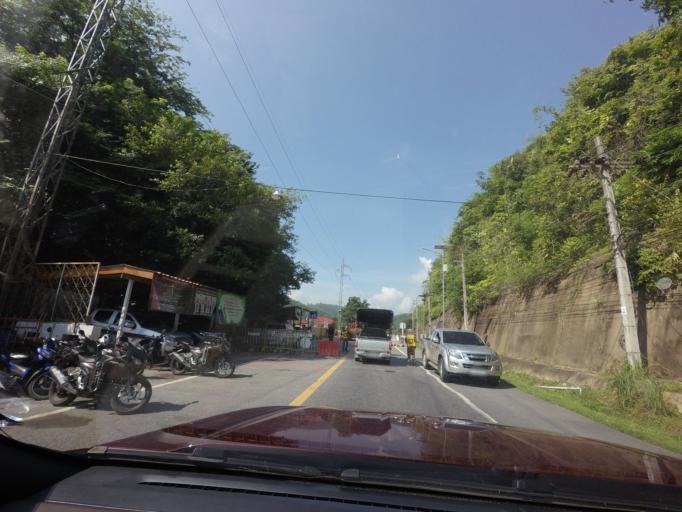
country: TH
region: Yala
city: Than To
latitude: 5.9626
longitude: 101.1949
